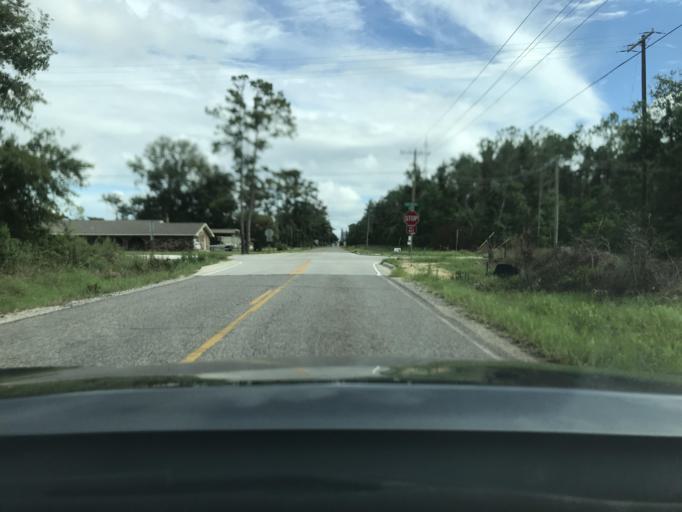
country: US
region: Louisiana
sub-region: Calcasieu Parish
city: Westlake
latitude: 30.2647
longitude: -93.2751
